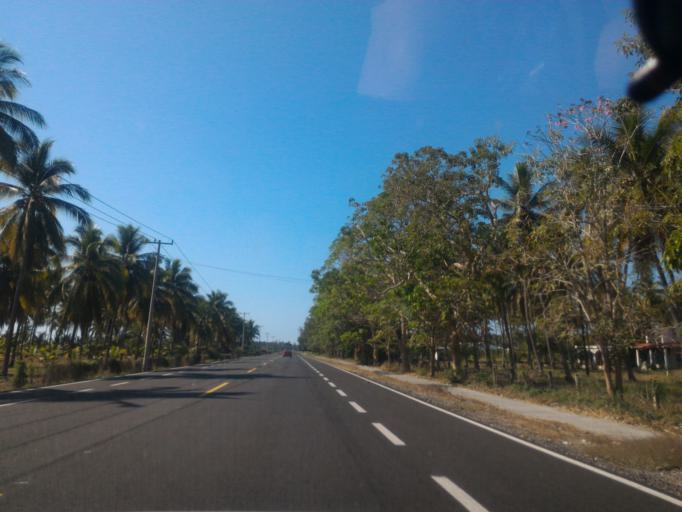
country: MX
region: Colima
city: Tecoman
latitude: 18.8823
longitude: -103.9245
